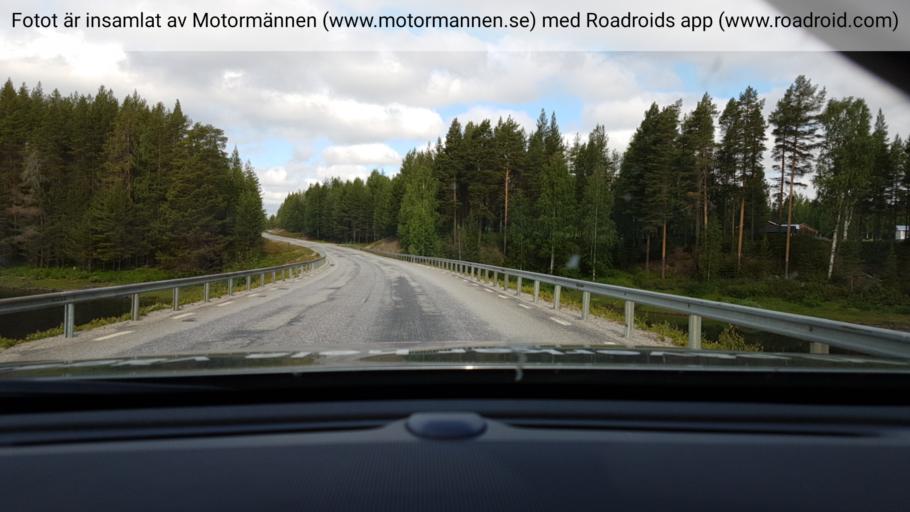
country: SE
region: Vaesterbotten
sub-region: Lycksele Kommun
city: Lycksele
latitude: 64.8515
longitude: 18.7575
